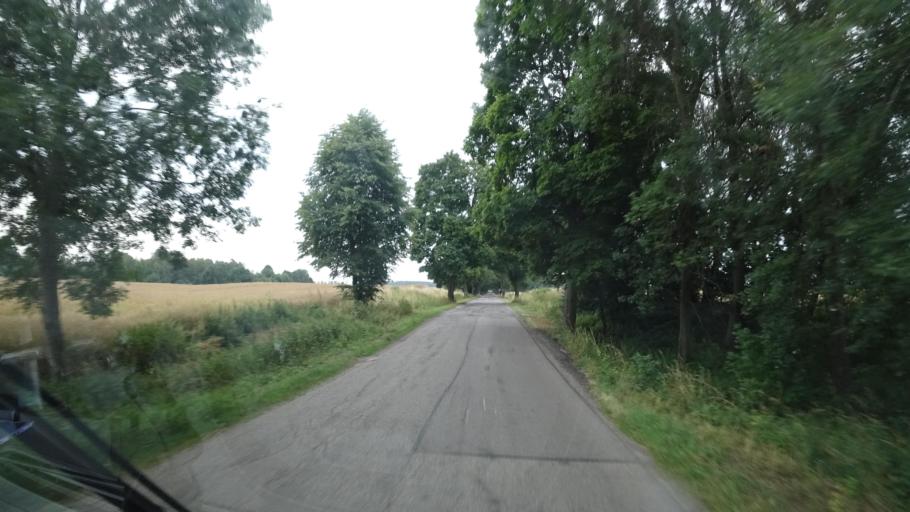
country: PL
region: Warmian-Masurian Voivodeship
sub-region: Powiat gizycki
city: Ryn
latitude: 53.9145
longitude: 21.5577
